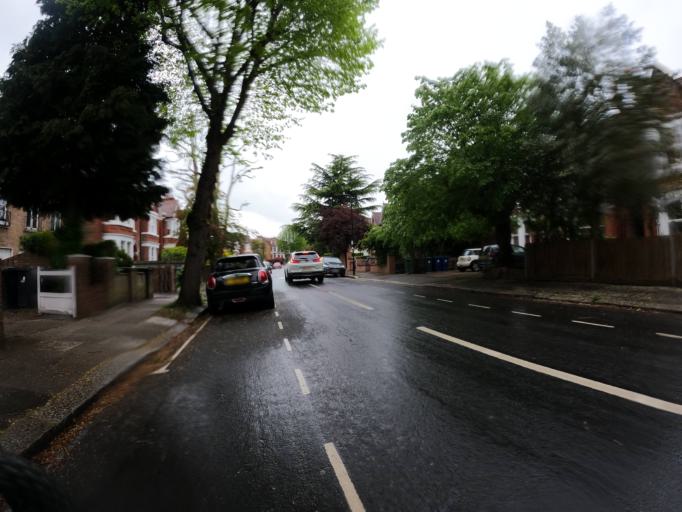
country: GB
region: England
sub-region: Greater London
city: Acton
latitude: 51.5122
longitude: -0.2856
